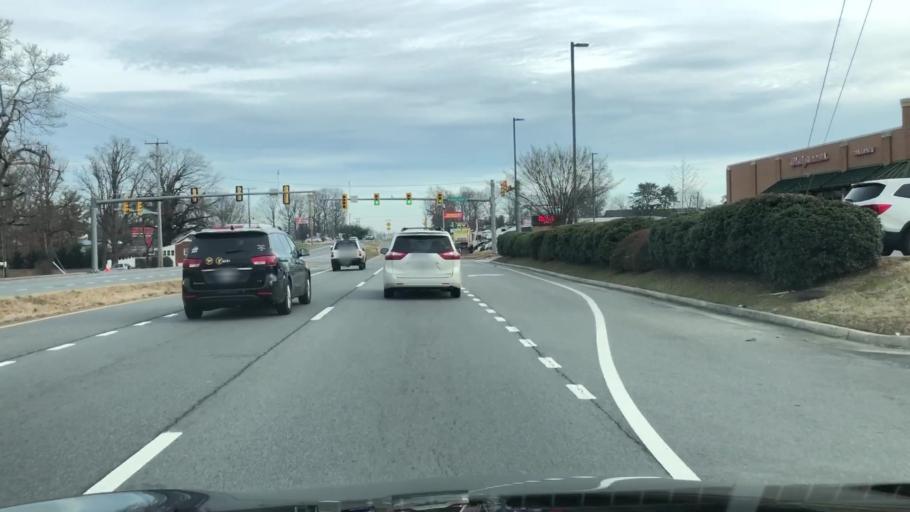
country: US
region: Virginia
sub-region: Campbell County
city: Timberlake
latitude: 37.3297
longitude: -79.2459
